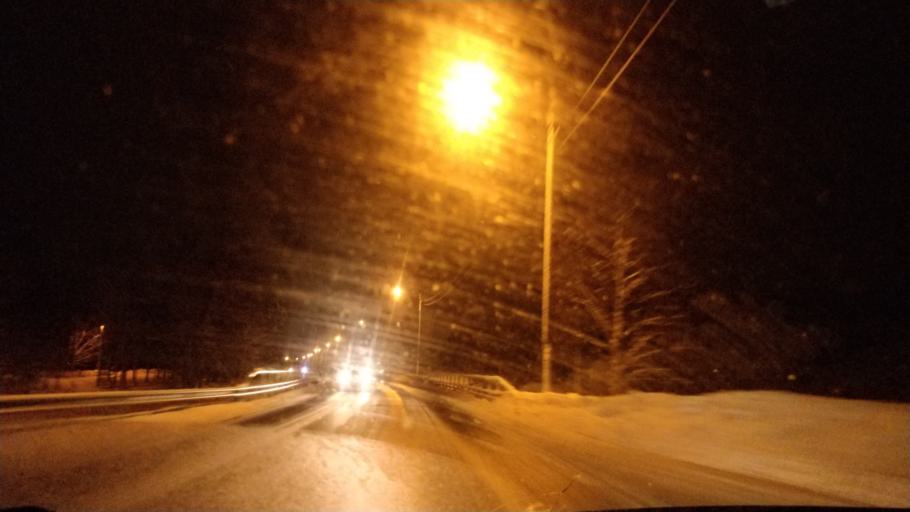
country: FI
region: Lapland
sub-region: Rovaniemi
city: Rovaniemi
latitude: 66.3922
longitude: 25.3798
